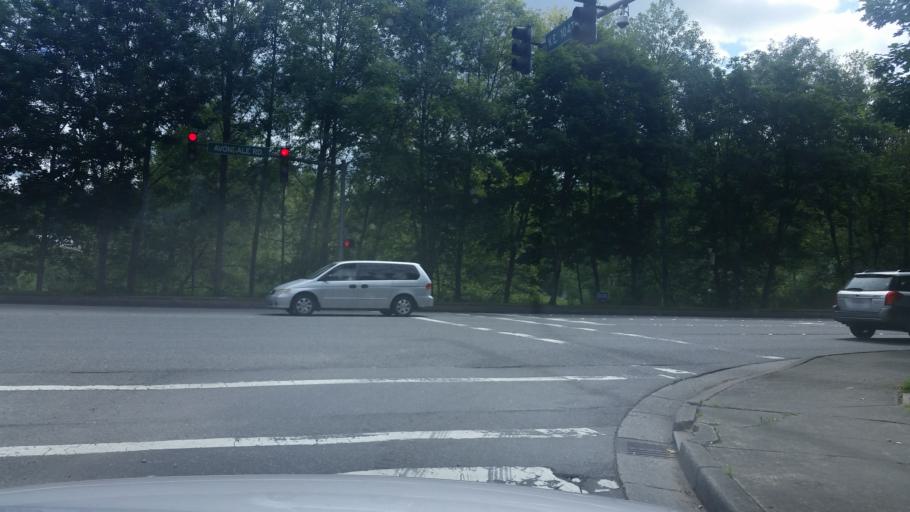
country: US
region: Washington
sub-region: King County
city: Redmond
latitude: 47.6928
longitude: -122.0931
